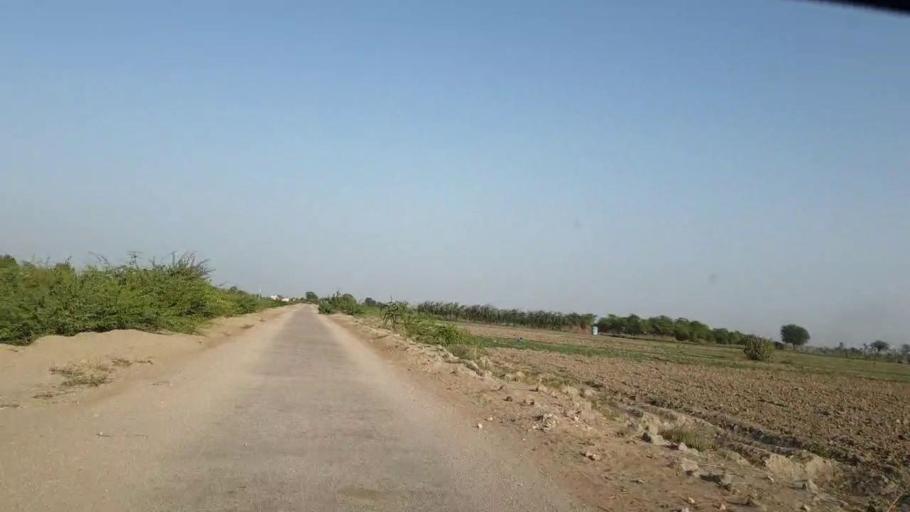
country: PK
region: Sindh
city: Kunri
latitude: 25.0779
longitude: 69.4399
